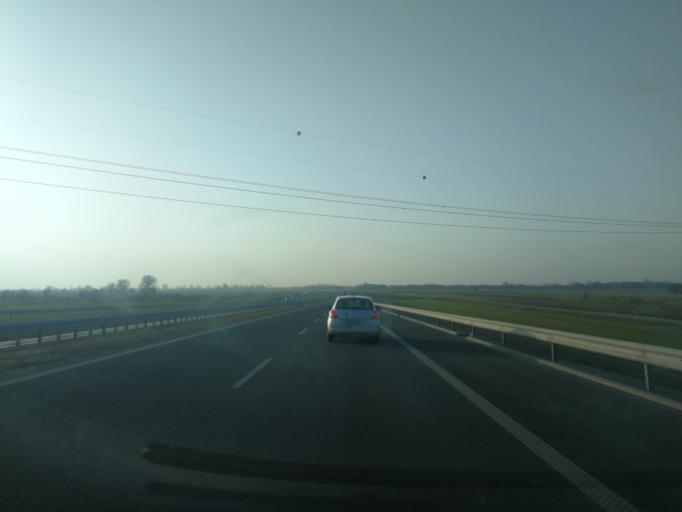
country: PL
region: Warmian-Masurian Voivodeship
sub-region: Powiat elblaski
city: Gronowo Elblaskie
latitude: 54.1675
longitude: 19.2343
